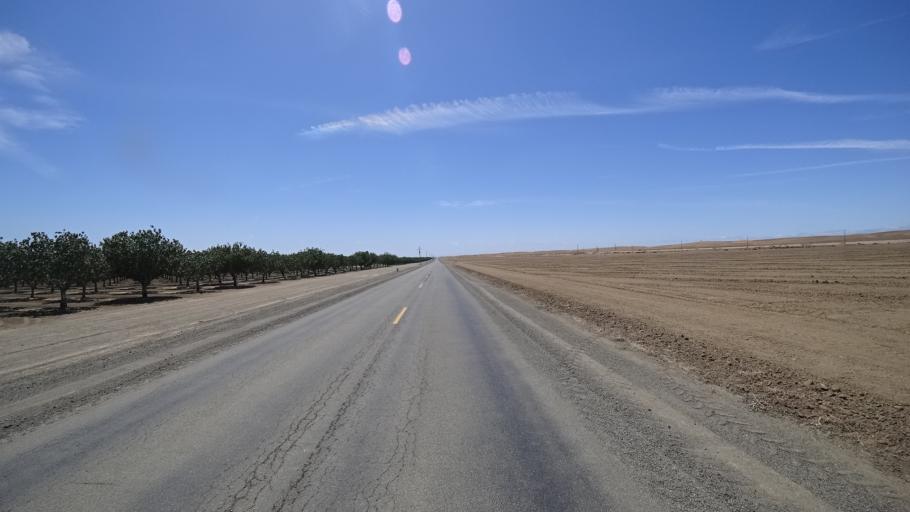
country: US
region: California
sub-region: Kings County
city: Kettleman City
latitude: 35.9219
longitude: -119.9149
